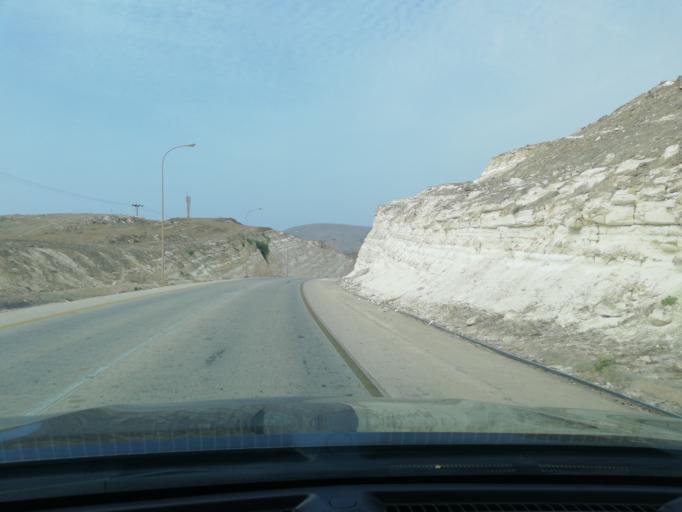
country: OM
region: Zufar
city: Salalah
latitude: 16.9180
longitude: 53.8422
